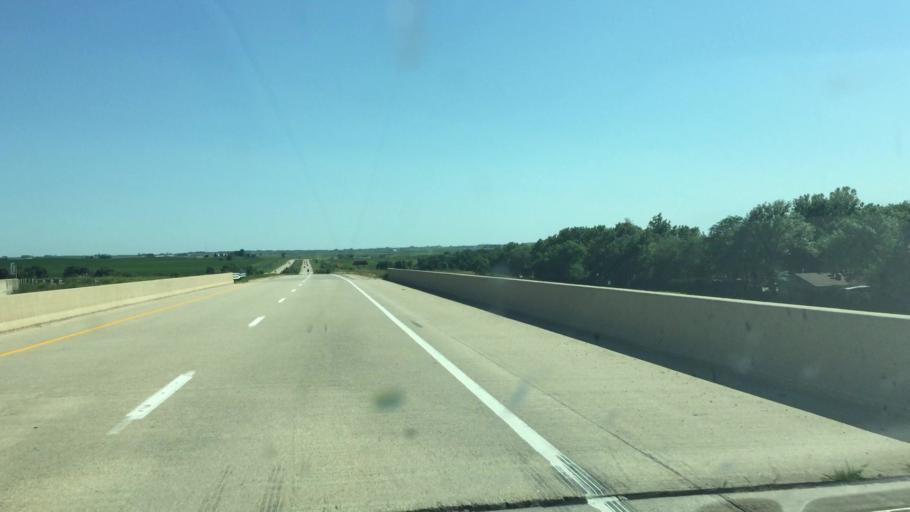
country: US
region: Iowa
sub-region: Jones County
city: Monticello
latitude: 42.2308
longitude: -91.1712
